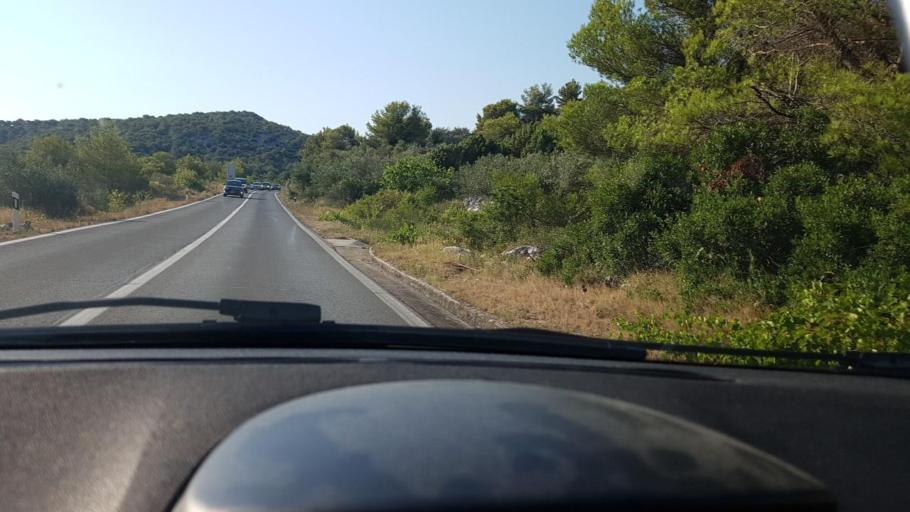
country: HR
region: Sibensko-Kniniska
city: Murter
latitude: 43.8058
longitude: 15.6085
